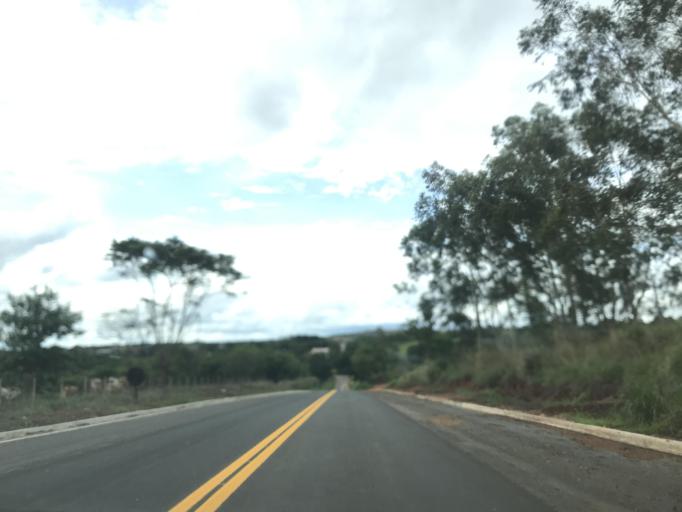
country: BR
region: Goias
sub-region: Bela Vista De Goias
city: Bela Vista de Goias
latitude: -17.0681
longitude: -48.6575
